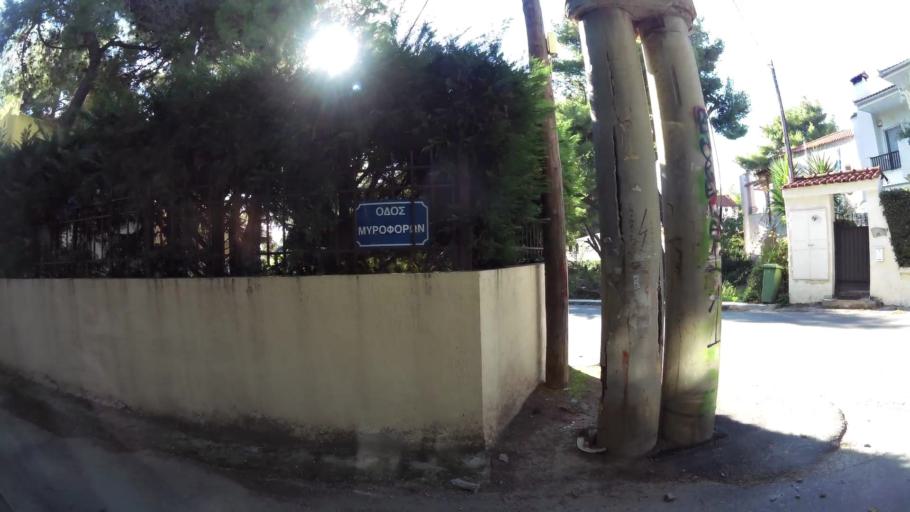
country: GR
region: Attica
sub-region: Nomarchia Athinas
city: Ekali
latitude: 38.1212
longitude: 23.8427
